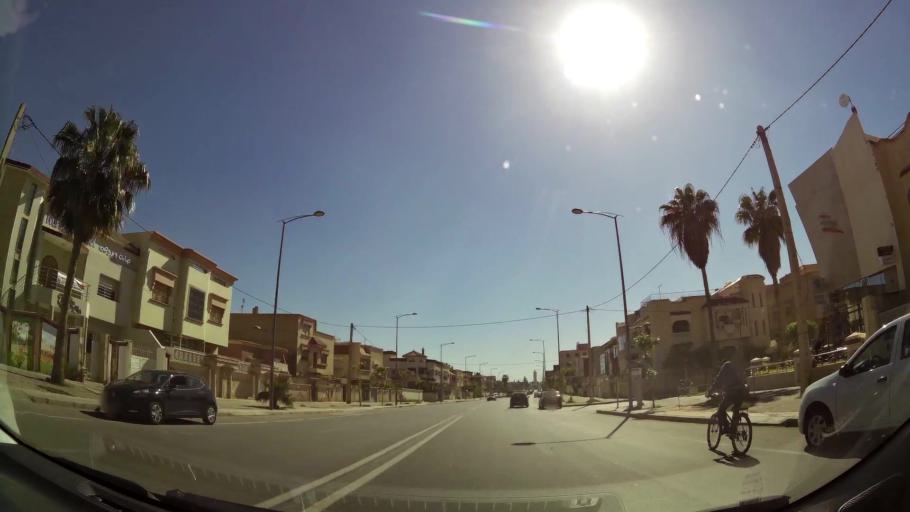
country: MA
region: Oriental
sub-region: Oujda-Angad
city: Oujda
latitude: 34.6649
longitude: -1.8937
